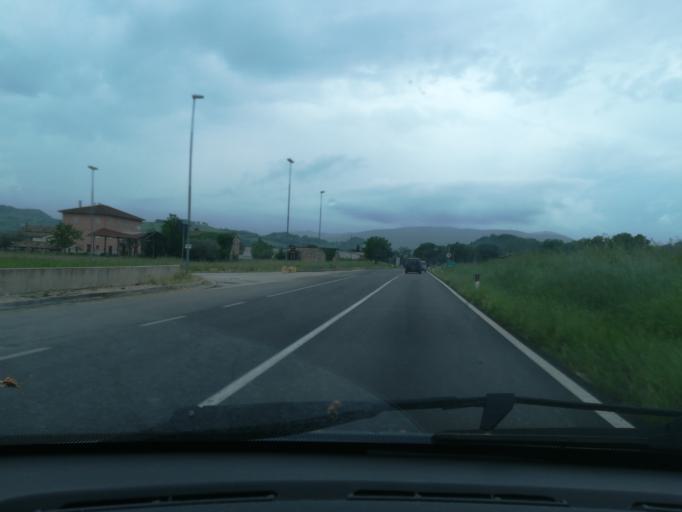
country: IT
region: The Marches
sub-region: Provincia di Macerata
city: San Severino Marche
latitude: 43.2495
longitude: 13.2282
